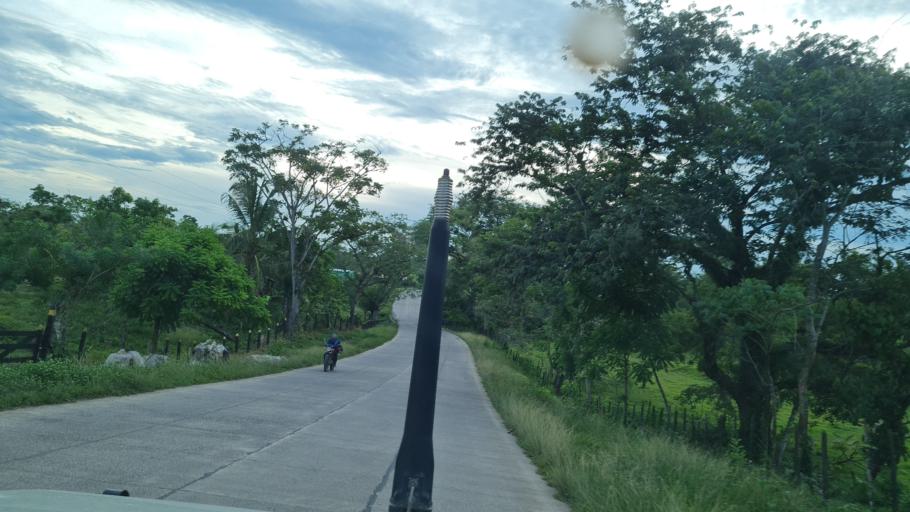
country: NI
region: Atlantico Norte (RAAN)
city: Siuna
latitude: 13.6840
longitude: -84.5931
